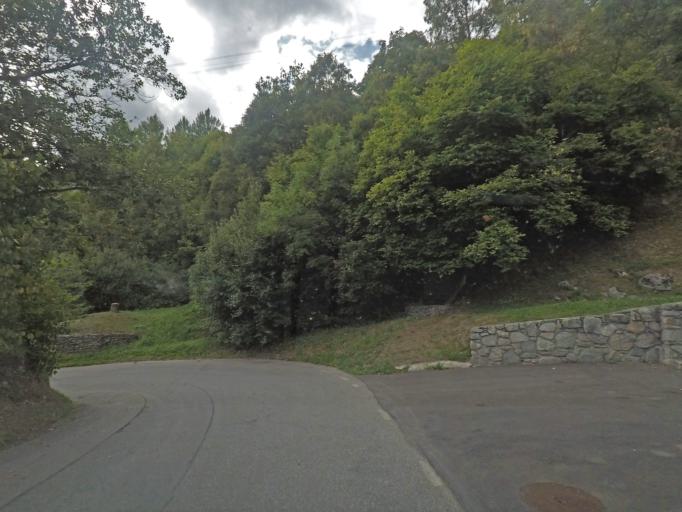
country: CH
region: Valais
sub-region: Brig District
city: Naters
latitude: 46.3623
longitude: 7.9837
